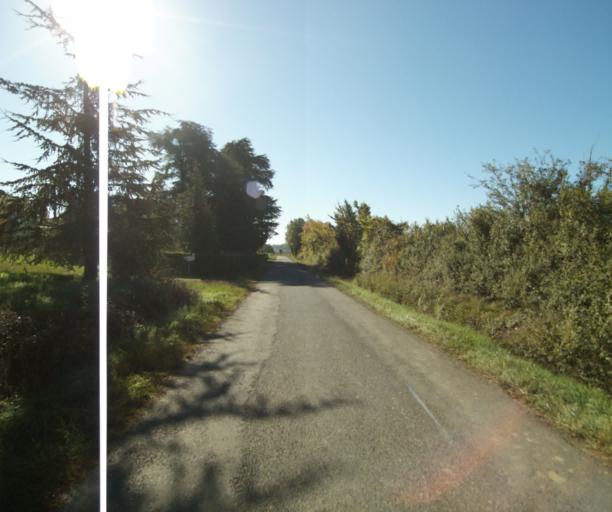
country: FR
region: Midi-Pyrenees
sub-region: Departement du Gers
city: Gondrin
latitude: 43.8201
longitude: 0.2186
